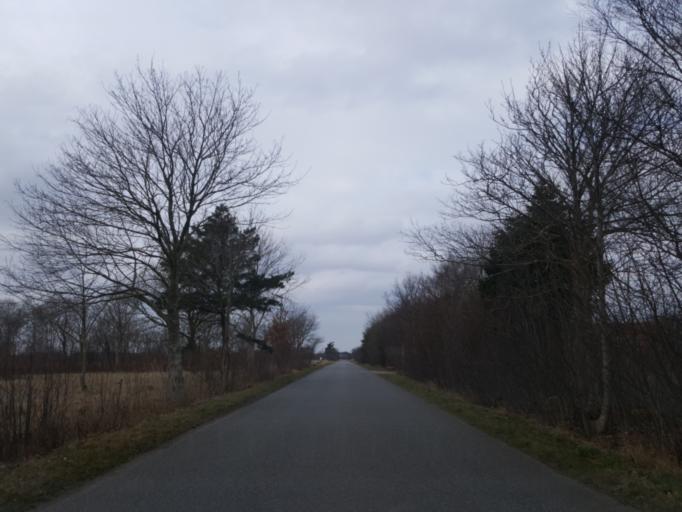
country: DK
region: Central Jutland
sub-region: Holstebro Kommune
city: Ulfborg
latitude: 56.3560
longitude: 8.2705
